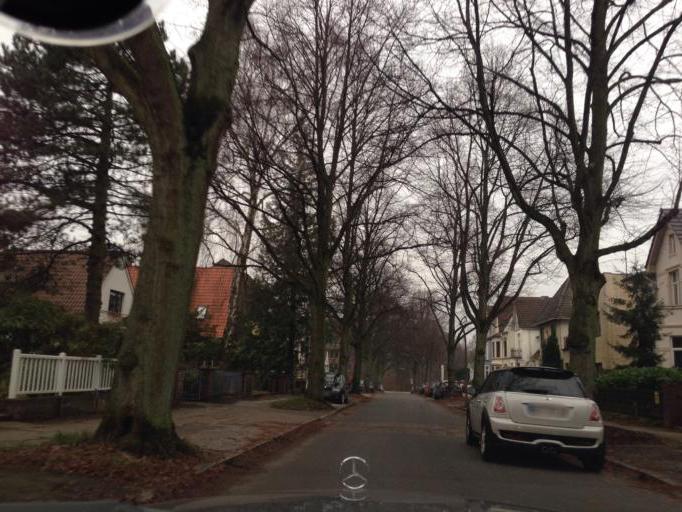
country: DE
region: Hamburg
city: Wandsbek
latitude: 53.5769
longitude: 10.0937
